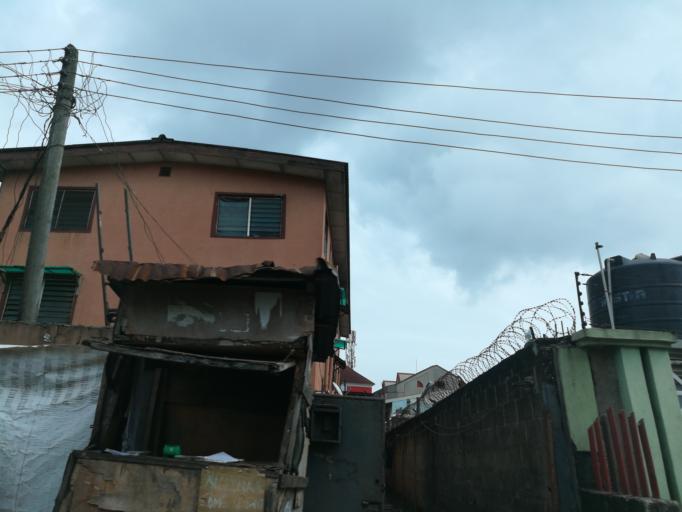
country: NG
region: Lagos
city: Ikeja
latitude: 6.6000
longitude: 3.3370
